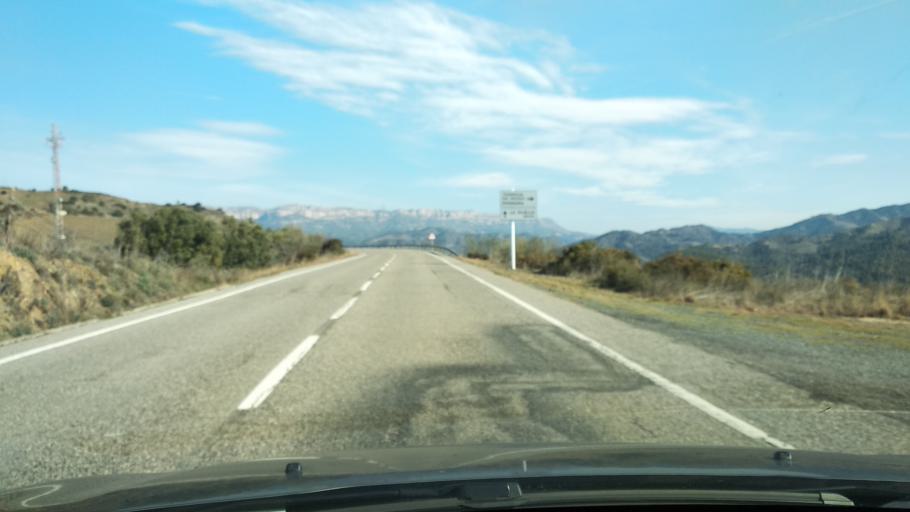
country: ES
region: Catalonia
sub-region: Provincia de Tarragona
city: Falset
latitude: 41.1985
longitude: 0.7811
